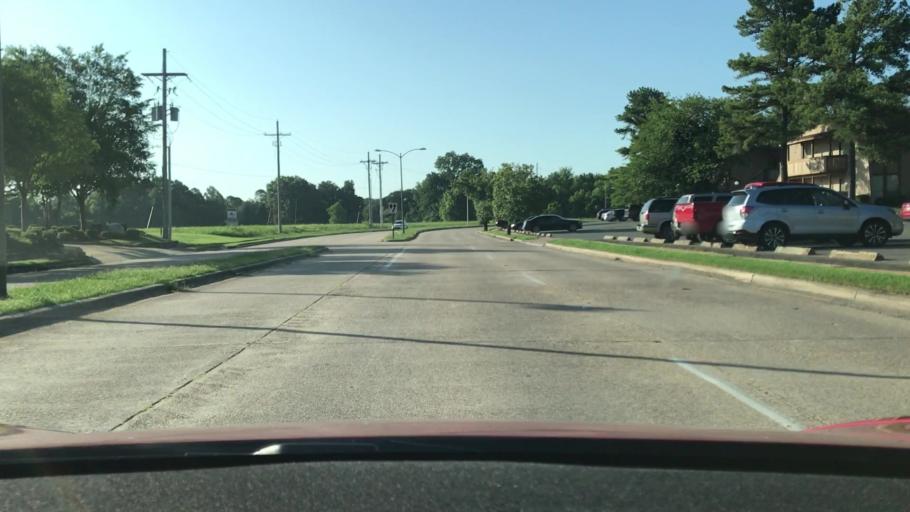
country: US
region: Louisiana
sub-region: Bossier Parish
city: Bossier City
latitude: 32.4419
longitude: -93.7292
